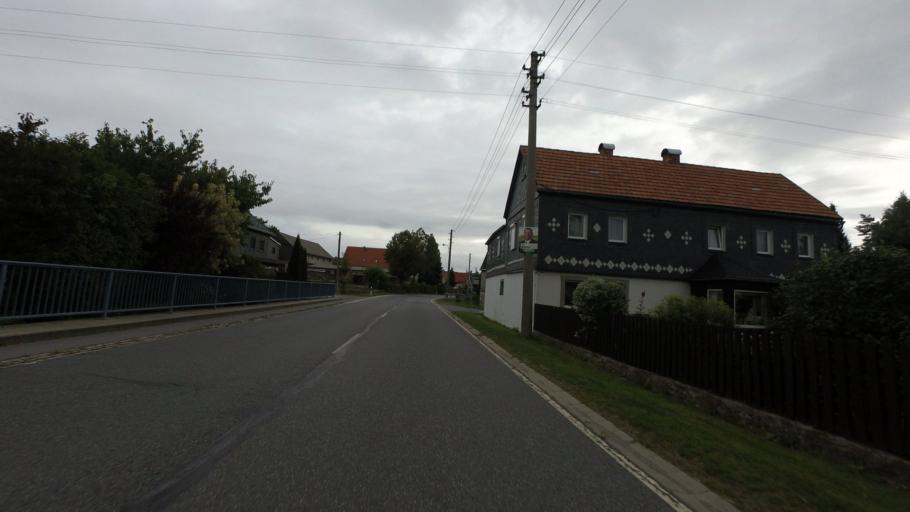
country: DE
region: Saxony
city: Berthelsdorf
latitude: 51.0534
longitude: 14.2270
